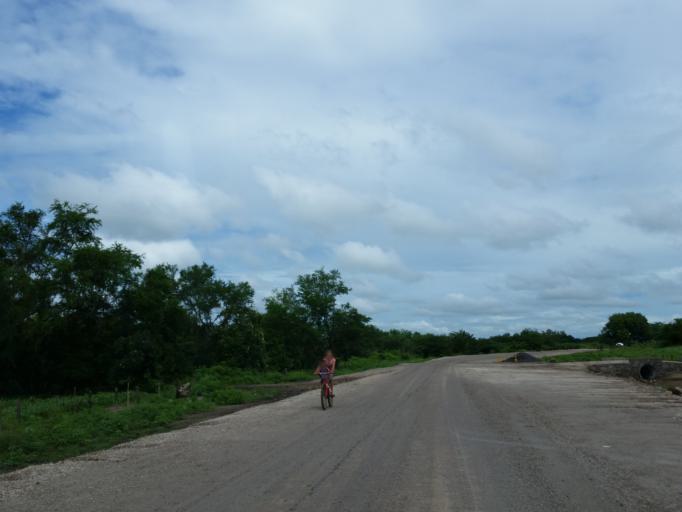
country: NI
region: Leon
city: Larreynaga
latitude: 12.5956
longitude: -86.6736
